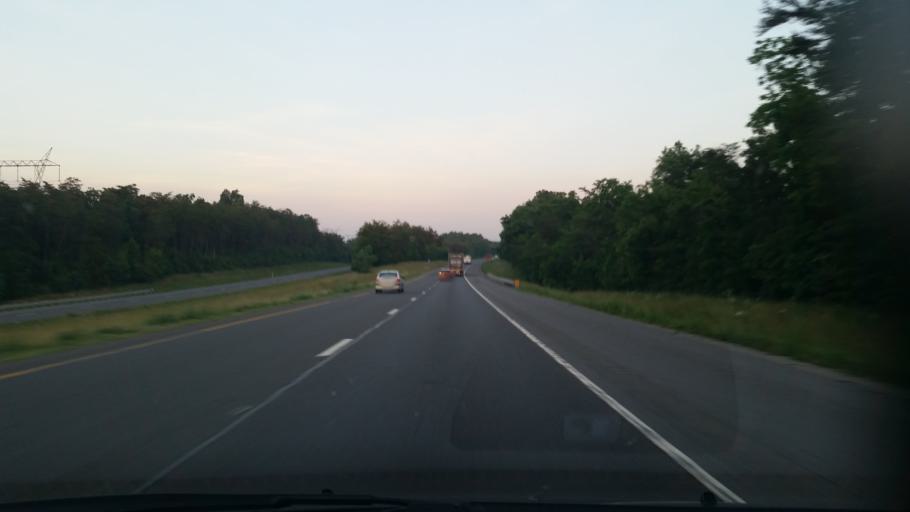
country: US
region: Tennessee
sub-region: Cumberland County
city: Crossville
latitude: 36.0404
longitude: -85.1112
